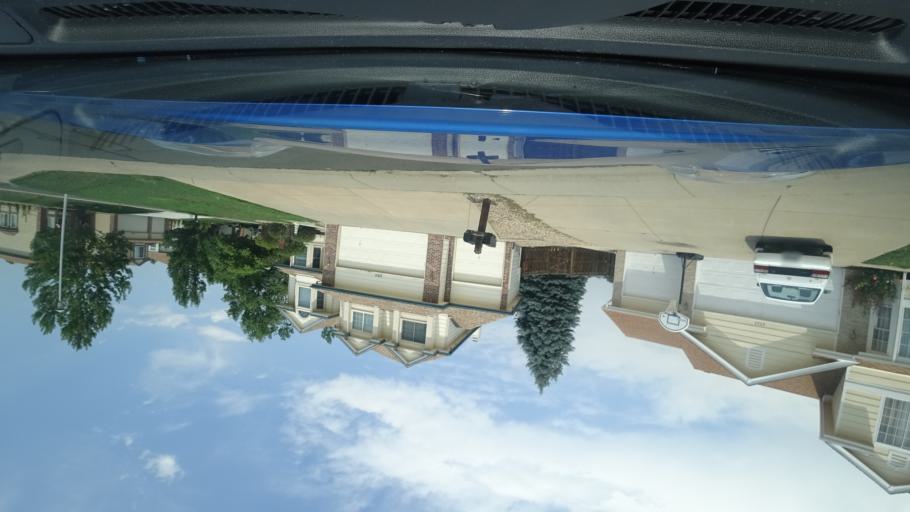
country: US
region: Colorado
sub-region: Adams County
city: Aurora
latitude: 39.6744
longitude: -104.7774
